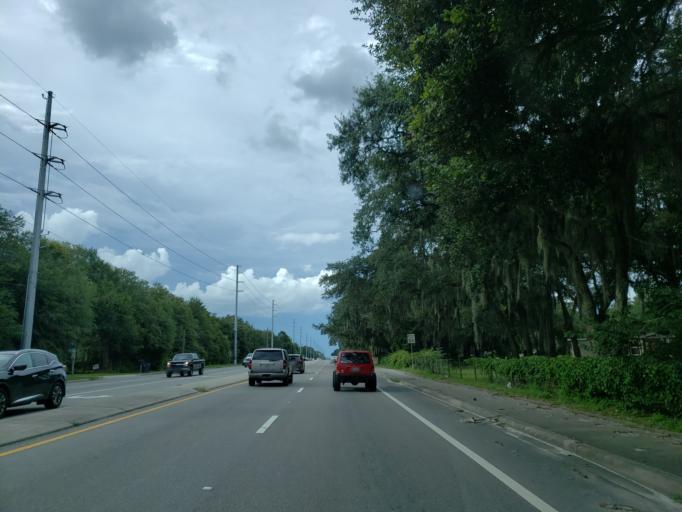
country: US
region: Florida
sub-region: Polk County
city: Willow Oak
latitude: 27.9384
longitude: -82.0552
